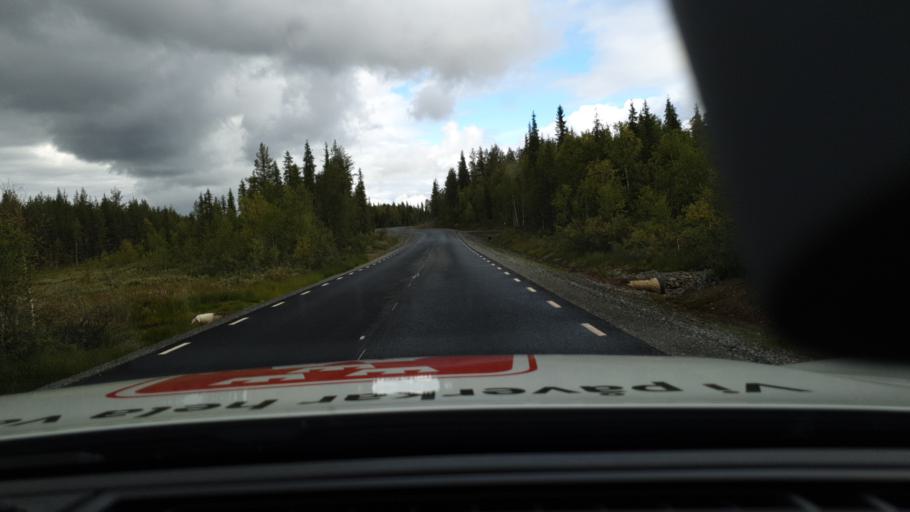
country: SE
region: Norrbotten
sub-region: Gallivare Kommun
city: Gaellivare
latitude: 66.8425
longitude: 21.0653
